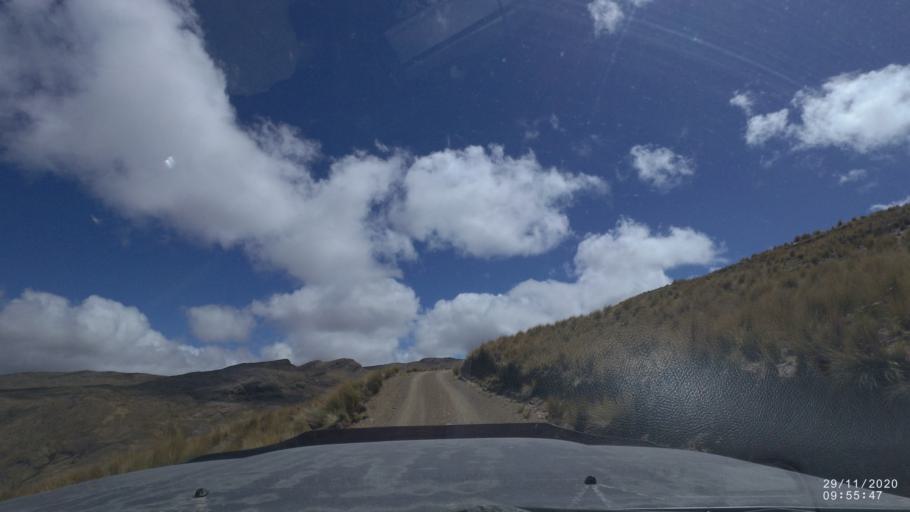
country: BO
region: Cochabamba
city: Cochabamba
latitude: -17.2736
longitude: -66.1772
